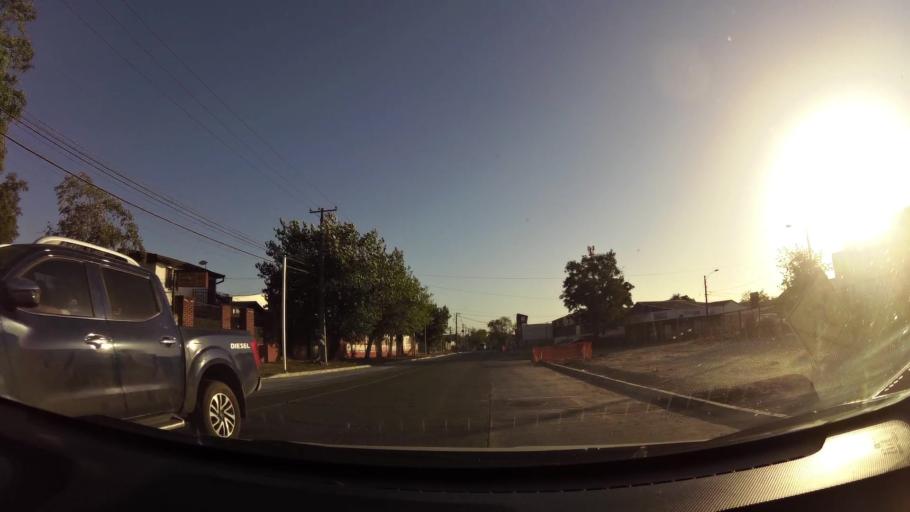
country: CL
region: Maule
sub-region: Provincia de Talca
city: Talca
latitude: -35.4355
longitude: -71.6427
